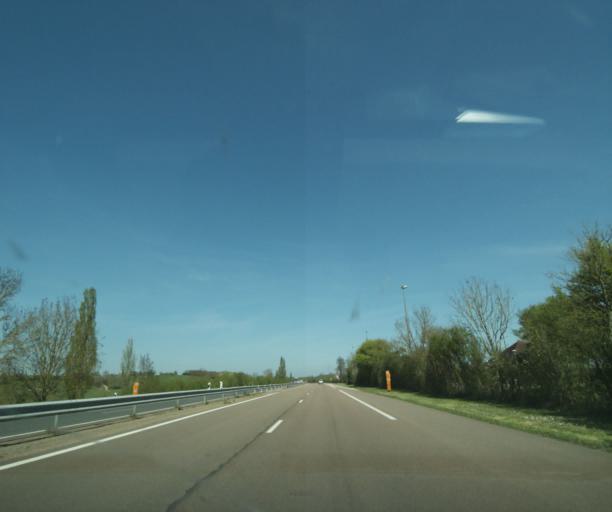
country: FR
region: Bourgogne
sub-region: Departement de la Nievre
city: La Charite-sur-Loire
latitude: 47.1559
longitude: 3.0495
